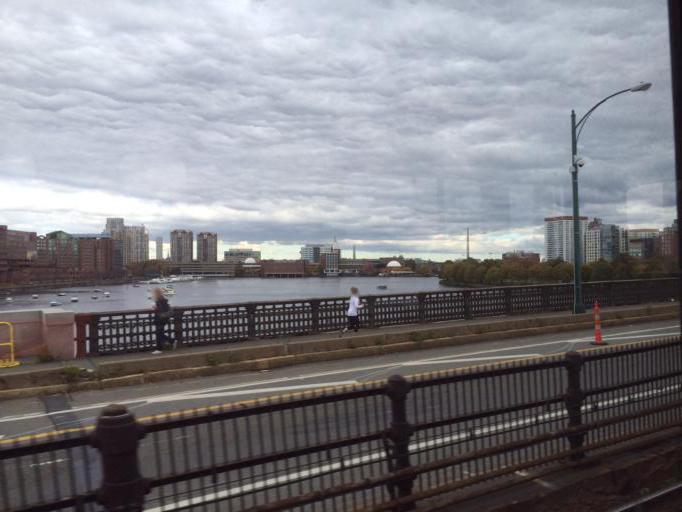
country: US
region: Massachusetts
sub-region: Suffolk County
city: Boston
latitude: 42.3616
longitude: -71.0767
